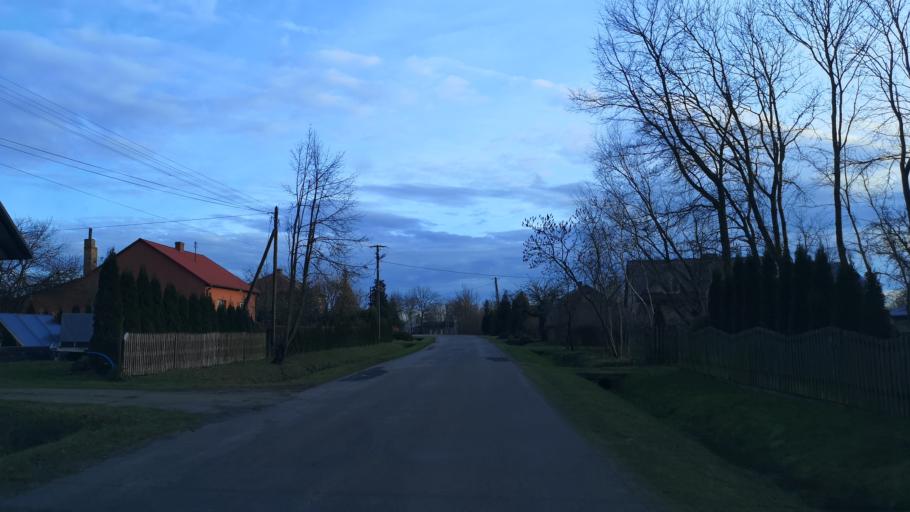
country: PL
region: Subcarpathian Voivodeship
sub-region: Powiat przeworski
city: Adamowka
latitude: 50.2421
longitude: 22.6379
